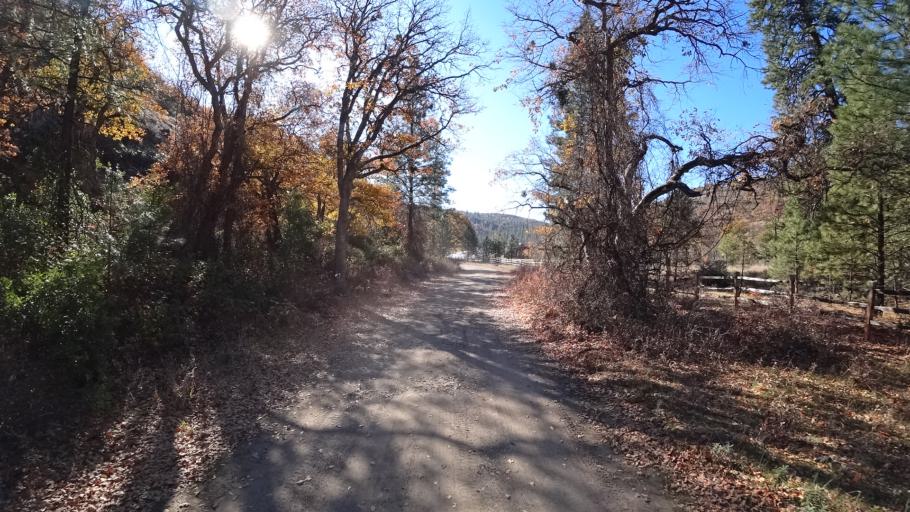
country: US
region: California
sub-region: Siskiyou County
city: Yreka
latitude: 41.8661
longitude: -122.8175
